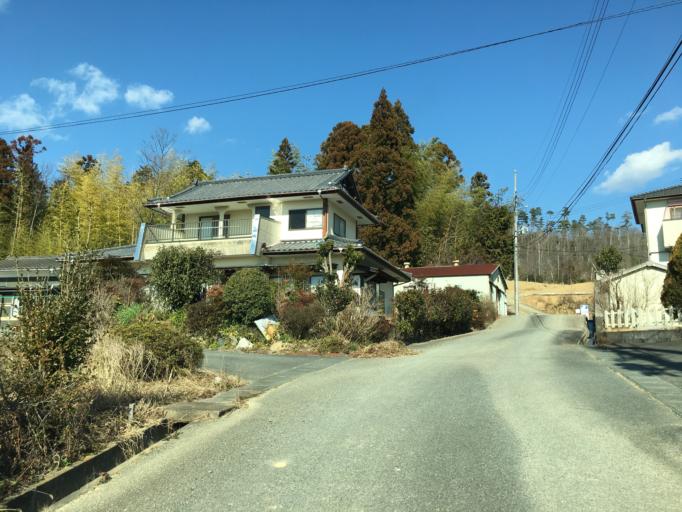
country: JP
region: Fukushima
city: Iwaki
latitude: 37.1745
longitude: 140.9618
